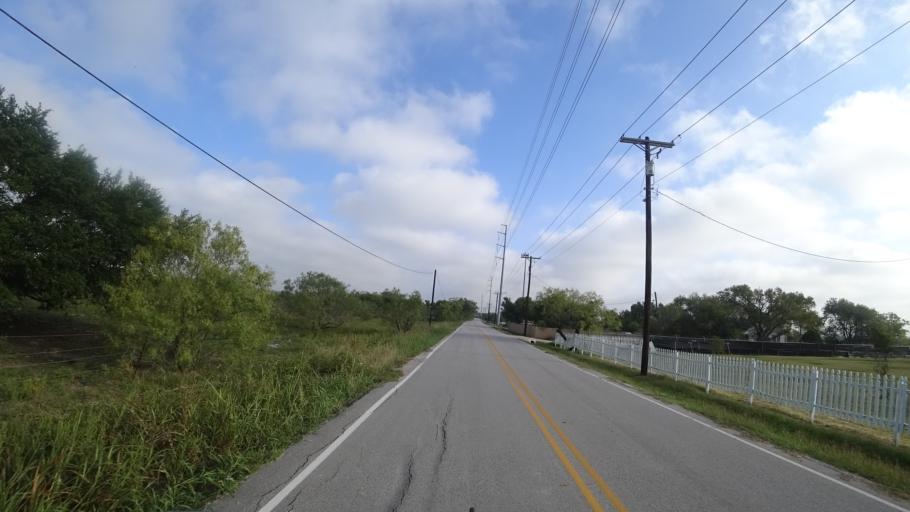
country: US
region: Texas
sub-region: Travis County
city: Pflugerville
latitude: 30.3640
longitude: -97.6294
